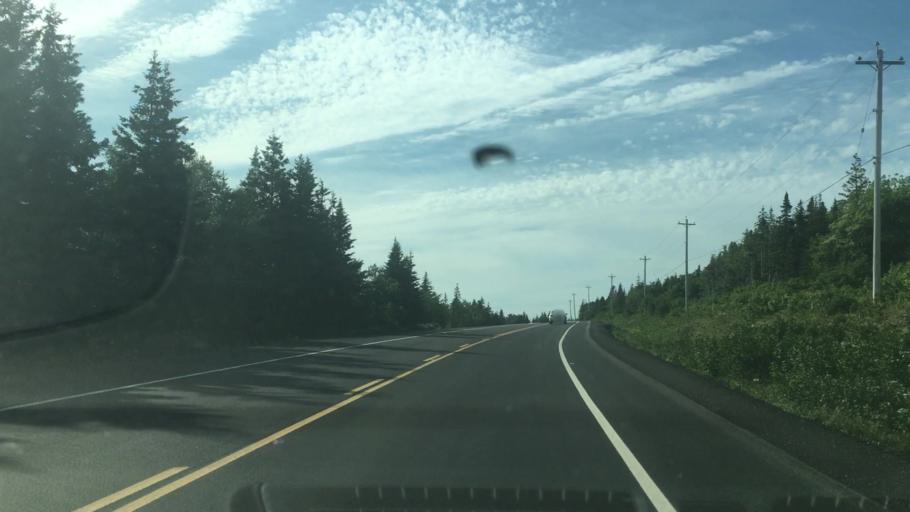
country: CA
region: Nova Scotia
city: Sydney Mines
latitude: 46.8435
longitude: -60.4031
